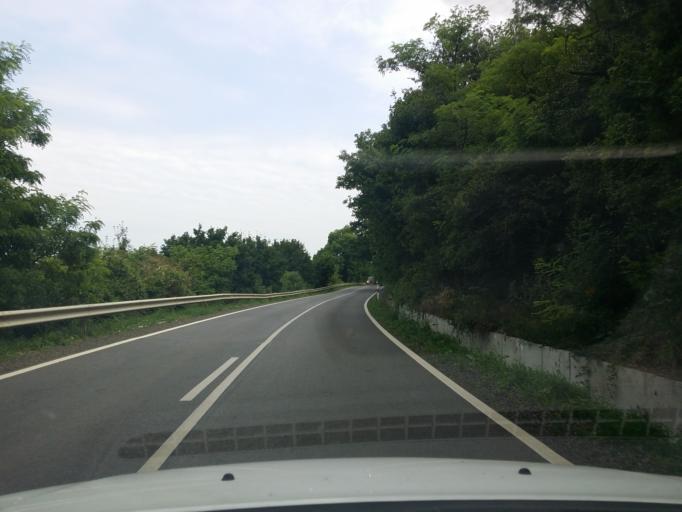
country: HU
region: Pest
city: Acsa
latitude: 47.7678
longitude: 19.3703
